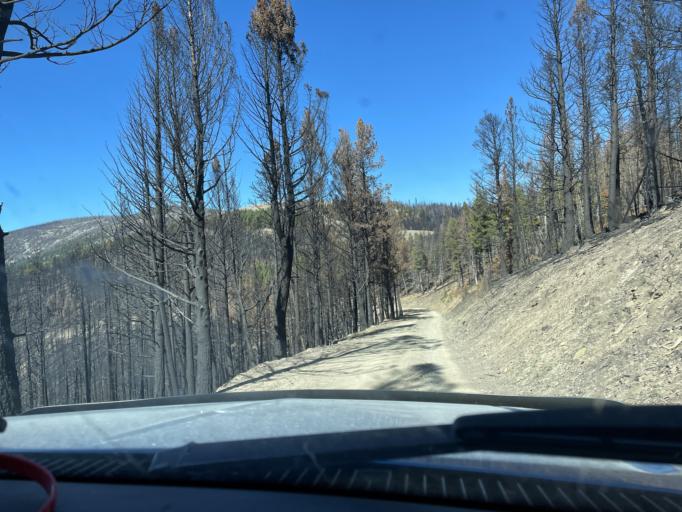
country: US
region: Montana
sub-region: Broadwater County
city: Townsend
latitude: 46.5045
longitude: -111.2754
